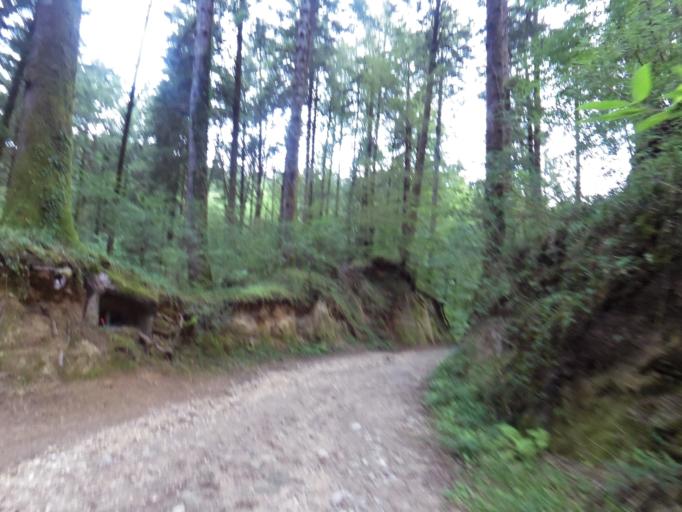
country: IT
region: Calabria
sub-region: Provincia di Vibo-Valentia
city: Serra San Bruno
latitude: 38.5524
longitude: 16.3109
